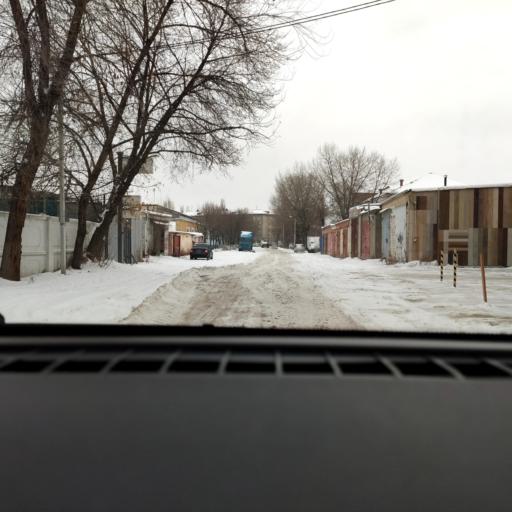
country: RU
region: Voronezj
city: Voronezh
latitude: 51.6336
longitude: 39.2509
